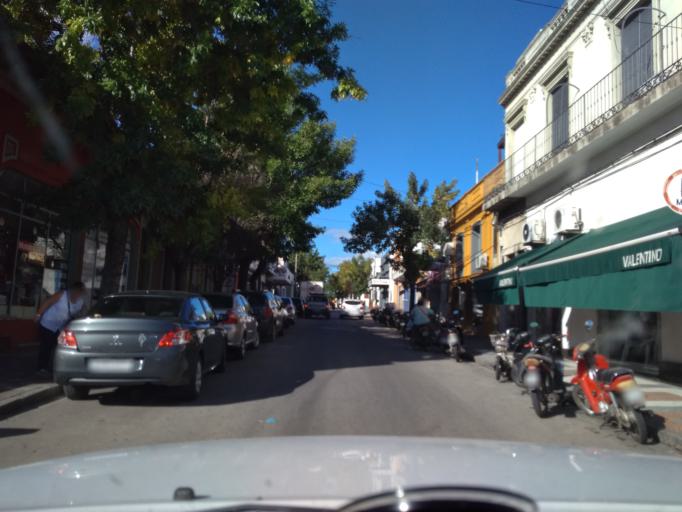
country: UY
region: Florida
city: Florida
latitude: -34.0970
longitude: -56.2170
